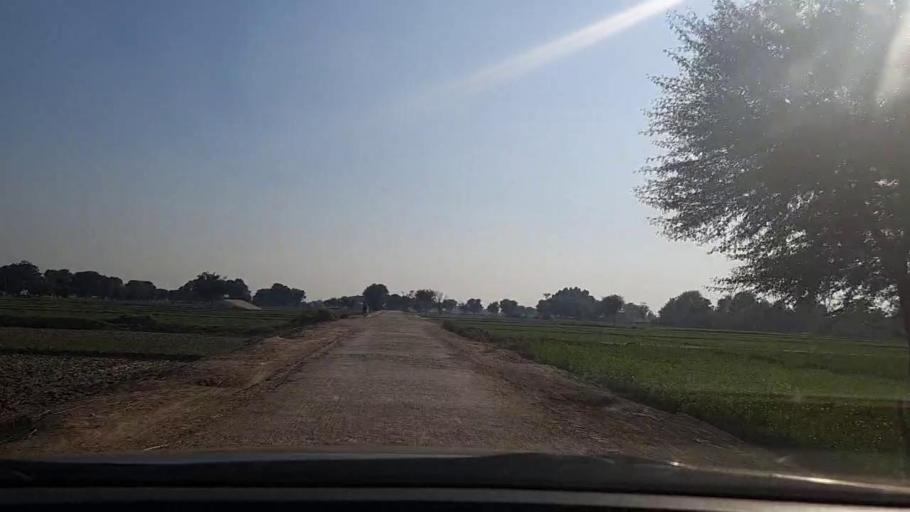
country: PK
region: Sindh
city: Sehwan
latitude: 26.3228
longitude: 68.0063
